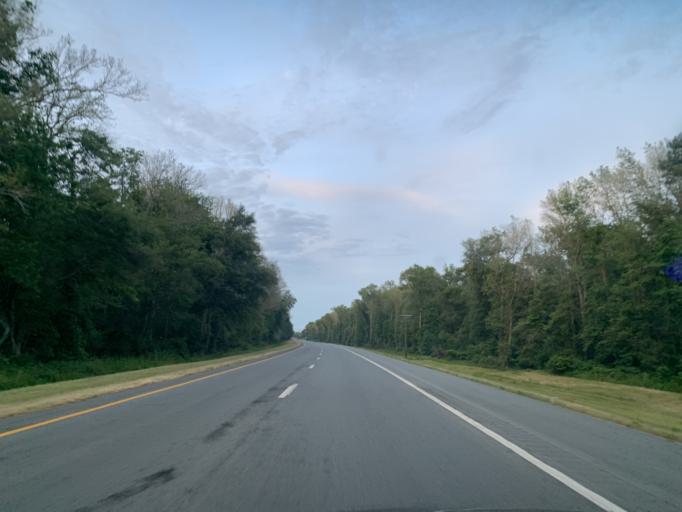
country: US
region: Maryland
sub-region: Wicomico County
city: Pittsville
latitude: 38.3841
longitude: -75.3346
